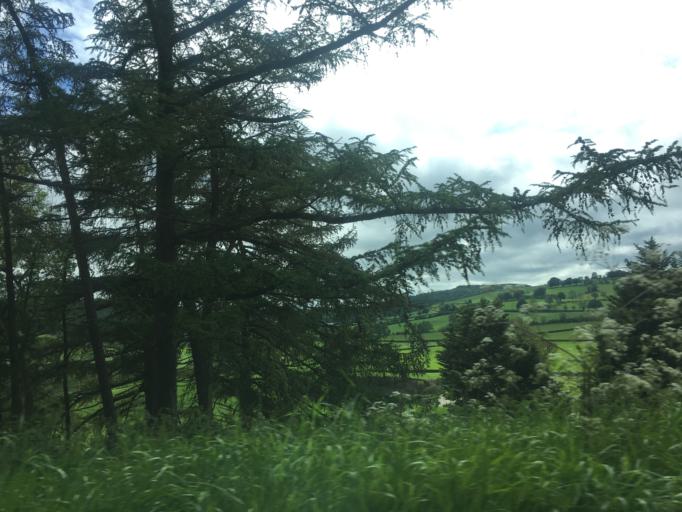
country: GB
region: Wales
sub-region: County of Ceredigion
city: Llangybi
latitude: 52.1412
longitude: -4.0618
